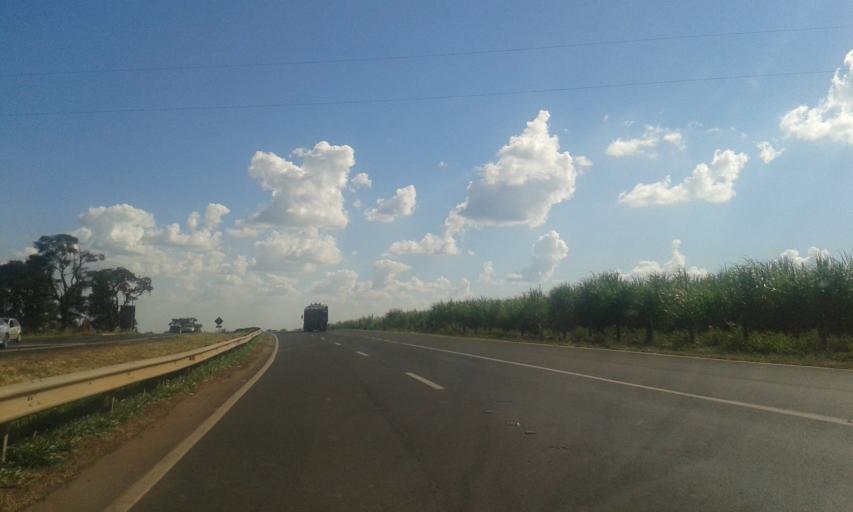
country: BR
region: Minas Gerais
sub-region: Monte Alegre De Minas
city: Monte Alegre de Minas
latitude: -18.8646
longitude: -48.5894
